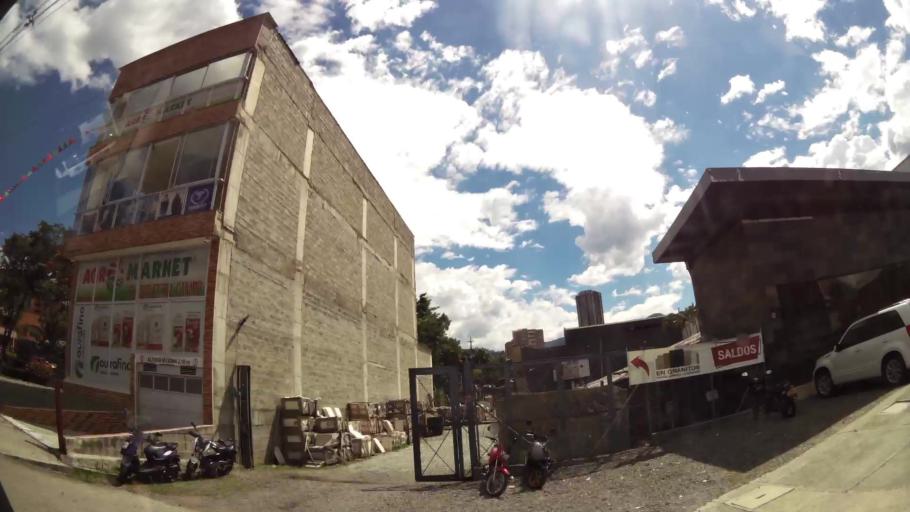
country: CO
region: Antioquia
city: Sabaneta
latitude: 6.1565
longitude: -75.6119
